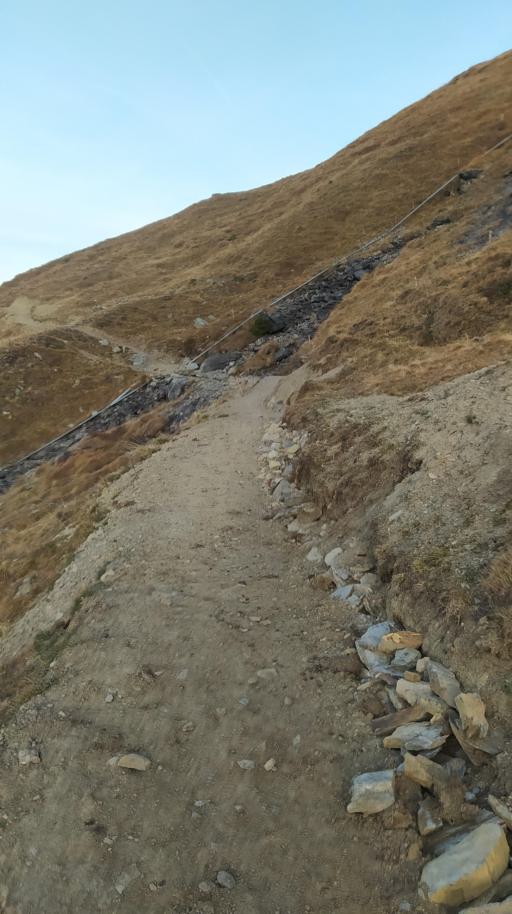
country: IT
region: Lombardy
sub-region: Provincia di Sondrio
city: Sant'Antonio
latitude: 46.4227
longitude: 10.5026
